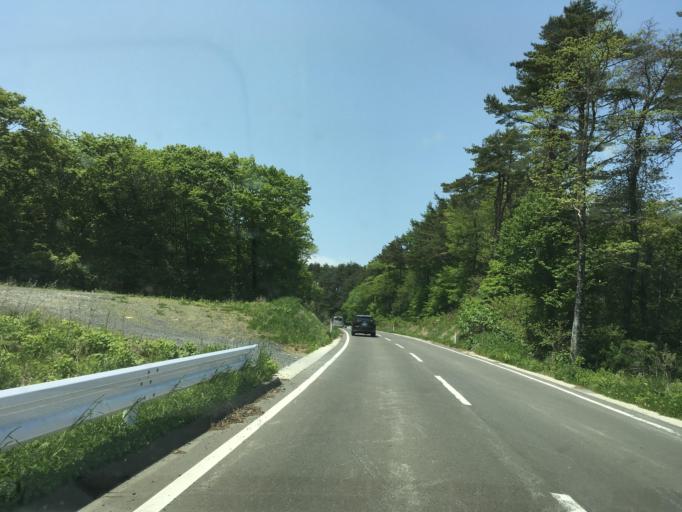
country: JP
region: Iwate
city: Ofunato
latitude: 38.8560
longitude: 141.4736
